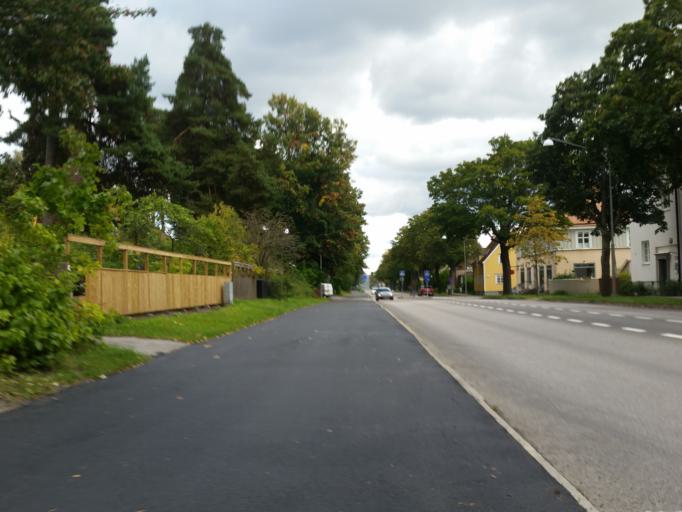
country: SE
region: Stockholm
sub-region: Stockholms Kommun
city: Arsta
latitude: 59.2836
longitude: 18.1006
